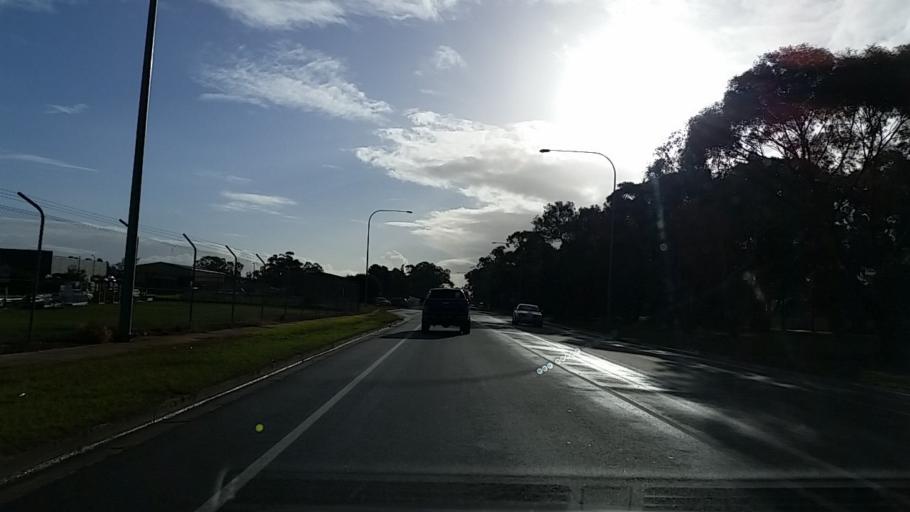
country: AU
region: South Australia
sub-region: Salisbury
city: Elizabeth
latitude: -34.6989
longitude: 138.6592
